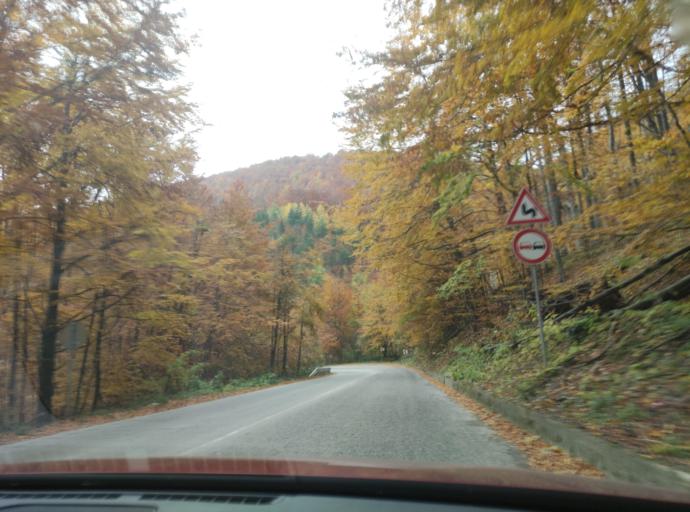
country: BG
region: Montana
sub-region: Obshtina Berkovitsa
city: Berkovitsa
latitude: 43.1359
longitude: 23.1422
